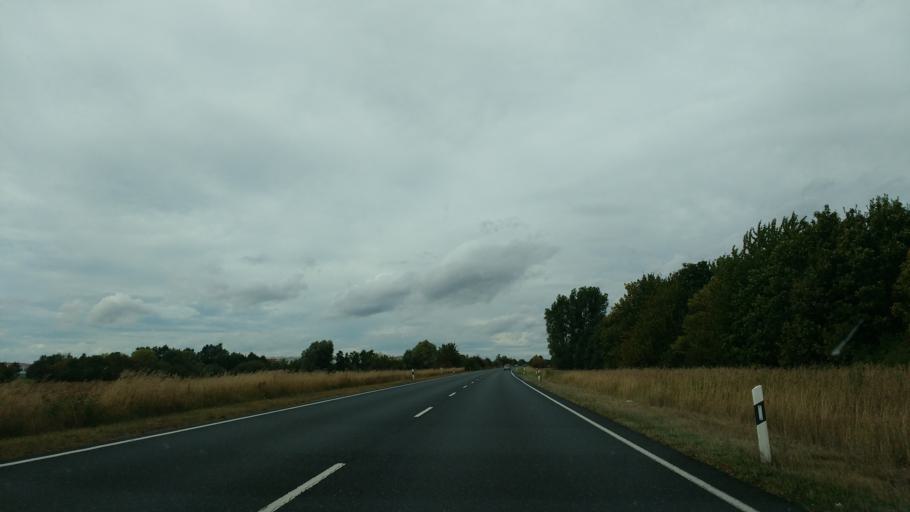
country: DE
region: Bavaria
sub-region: Regierungsbezirk Unterfranken
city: Schwebheim
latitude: 49.9795
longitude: 10.2491
